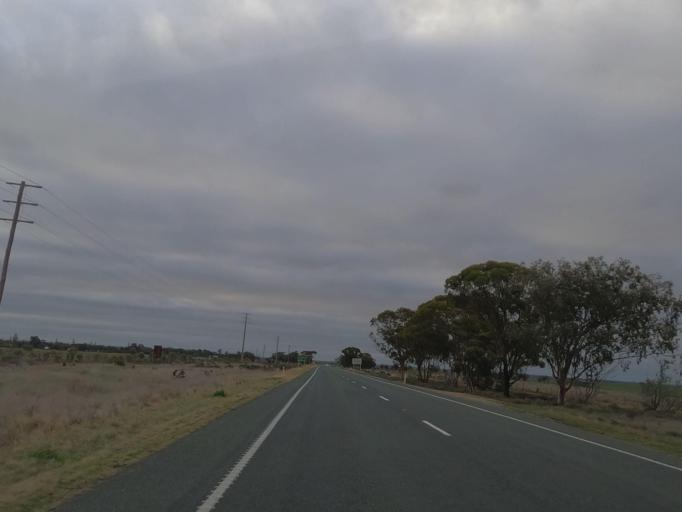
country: AU
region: Victoria
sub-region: Swan Hill
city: Swan Hill
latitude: -35.5688
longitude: 143.7851
